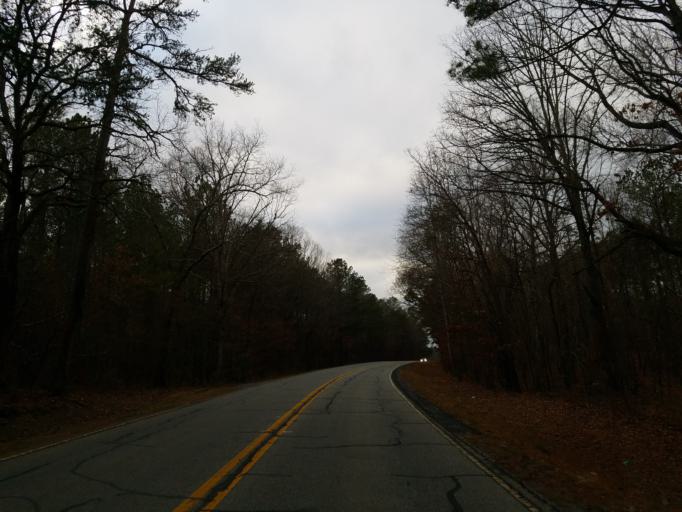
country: US
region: Georgia
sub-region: Bartow County
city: Rydal
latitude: 34.3472
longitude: -84.6804
